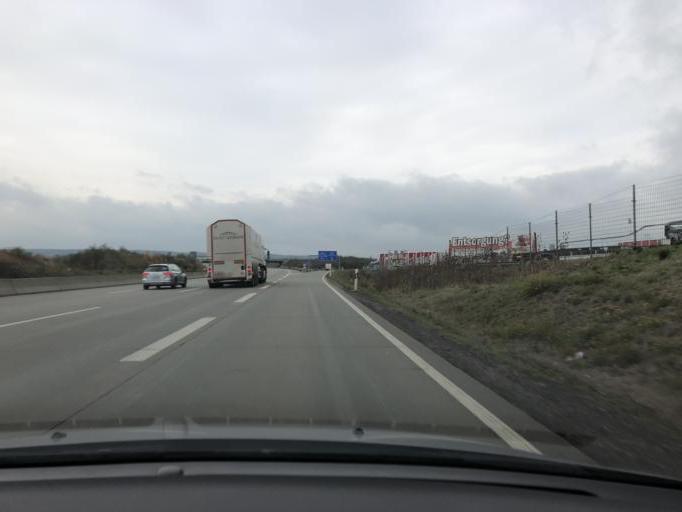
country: DE
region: Thuringia
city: Triptis
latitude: 50.7510
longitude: 11.8628
